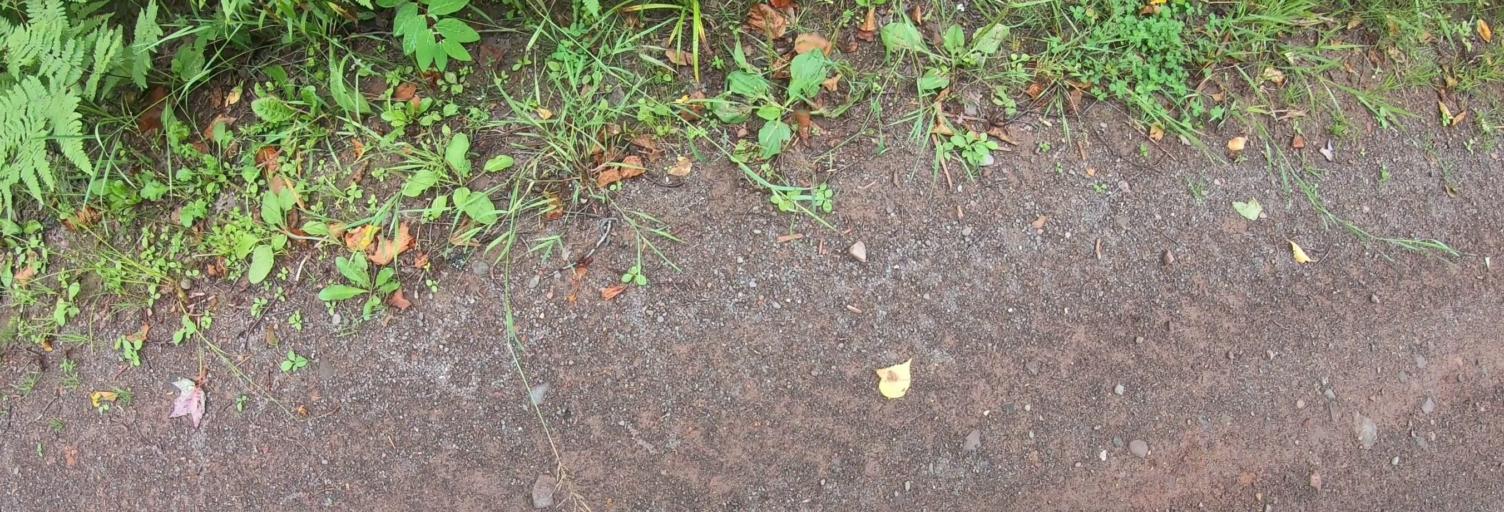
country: US
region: Michigan
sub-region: Keweenaw County
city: Eagle River
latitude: 47.2877
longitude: -88.2546
